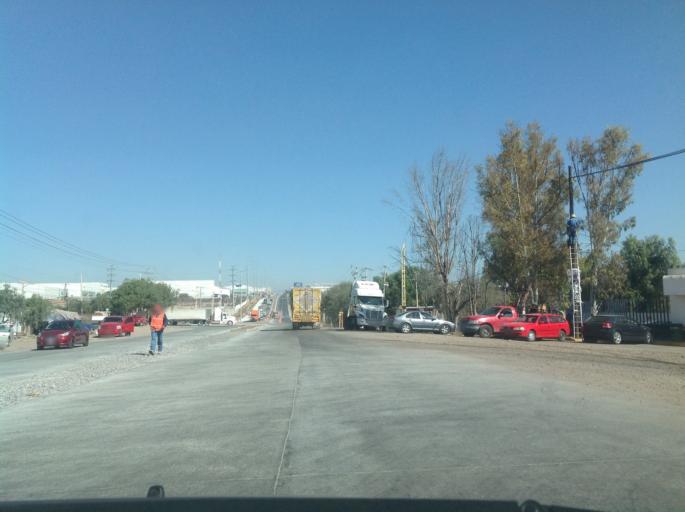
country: MX
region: Queretaro
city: El Colorado
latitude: 20.5487
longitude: -100.2666
